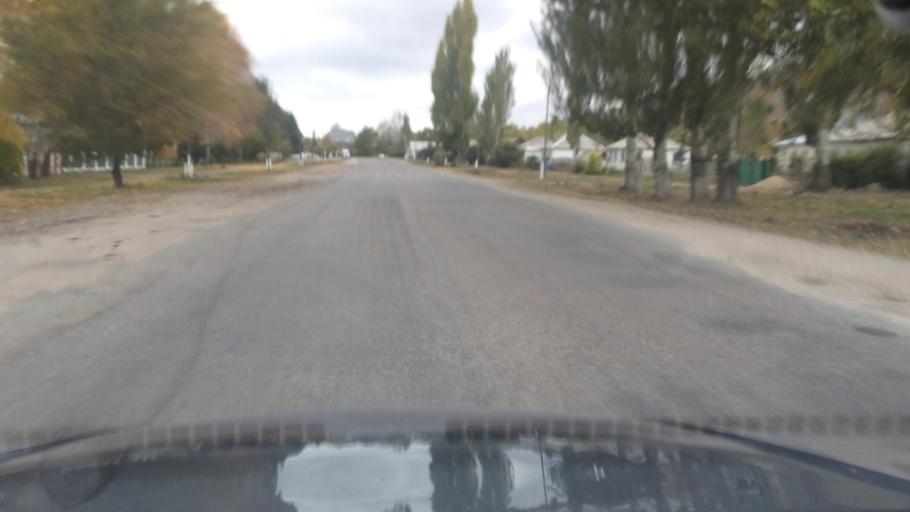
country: KG
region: Ysyk-Koel
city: Tyup
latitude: 42.7540
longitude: 78.1320
